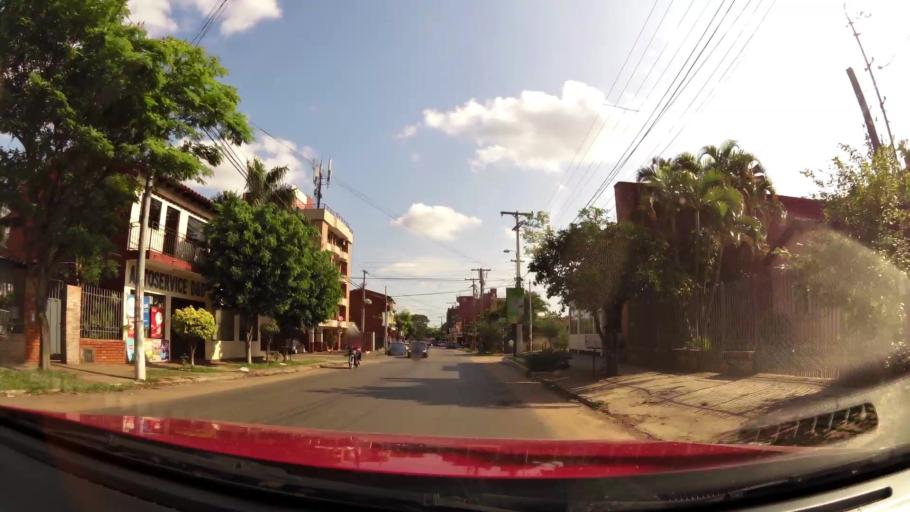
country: PY
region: Central
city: Fernando de la Mora
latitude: -25.3334
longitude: -57.5316
